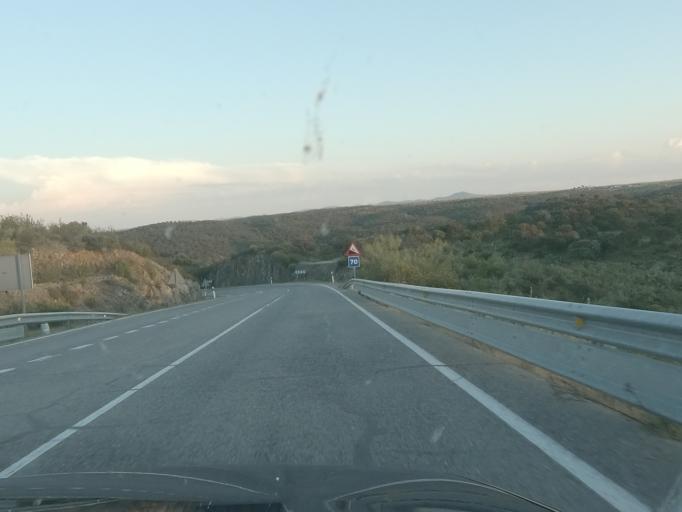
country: ES
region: Extremadura
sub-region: Provincia de Caceres
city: Salorino
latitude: 39.5685
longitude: -7.0045
